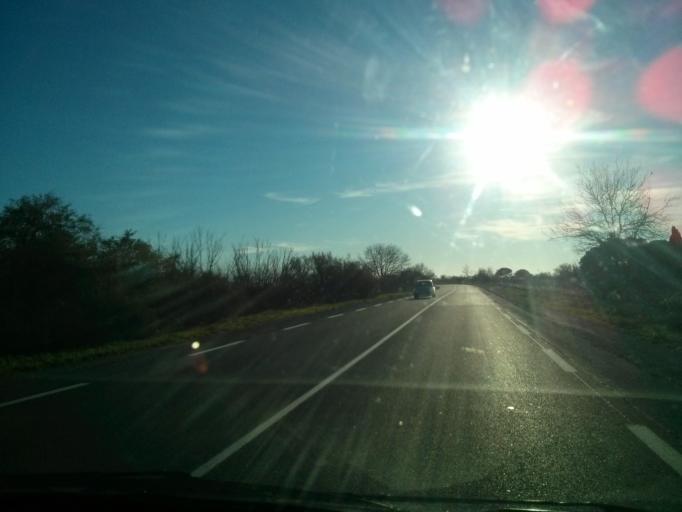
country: FR
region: Languedoc-Roussillon
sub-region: Departement de l'Herault
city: Candillargues
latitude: 43.6111
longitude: 4.1097
